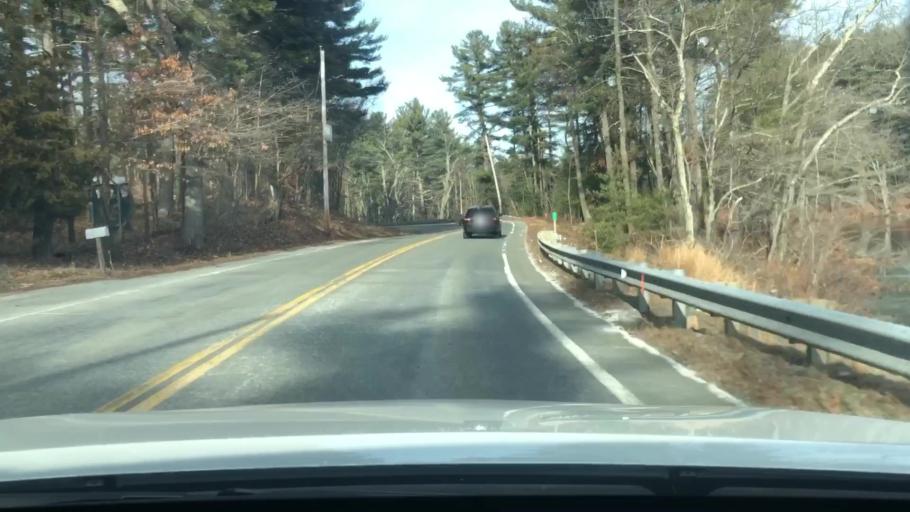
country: US
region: Massachusetts
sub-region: Worcester County
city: Grafton
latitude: 42.1938
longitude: -71.6562
